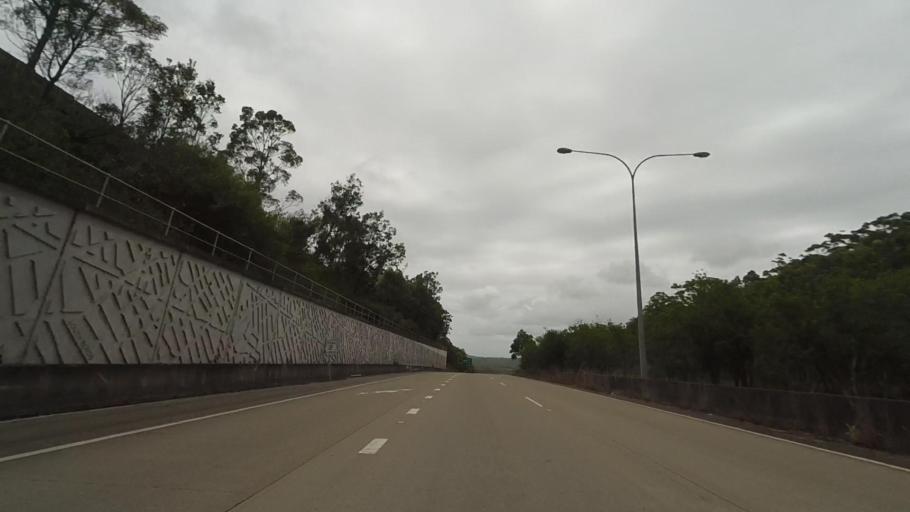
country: AU
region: New South Wales
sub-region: Lake Macquarie Shire
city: Kotara
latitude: -32.9506
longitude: 151.6838
